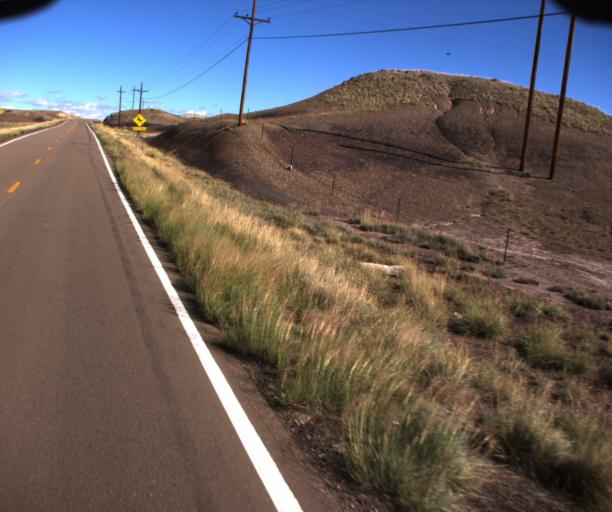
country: US
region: Arizona
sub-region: Apache County
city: Saint Johns
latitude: 34.5558
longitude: -109.3427
